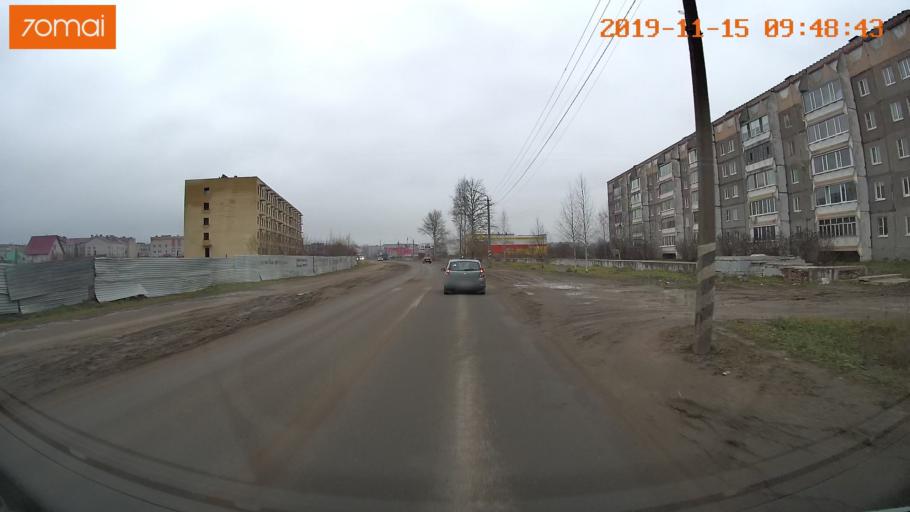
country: RU
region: Vologda
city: Sheksna
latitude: 59.2247
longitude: 38.5135
